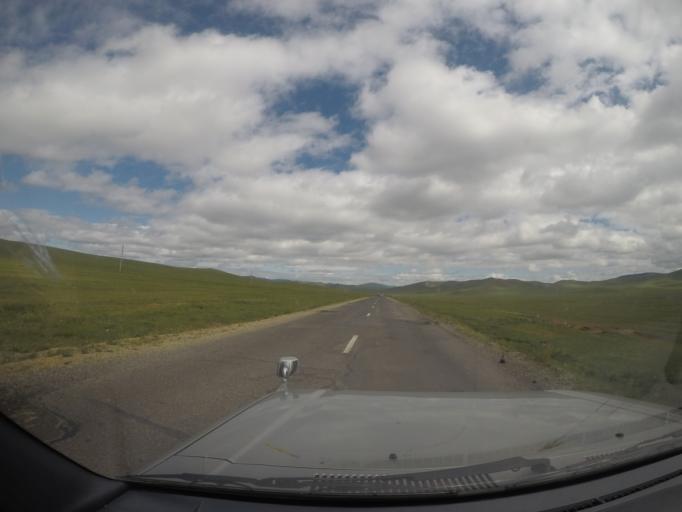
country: MN
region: Hentiy
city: Modot
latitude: 47.7676
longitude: 108.8846
